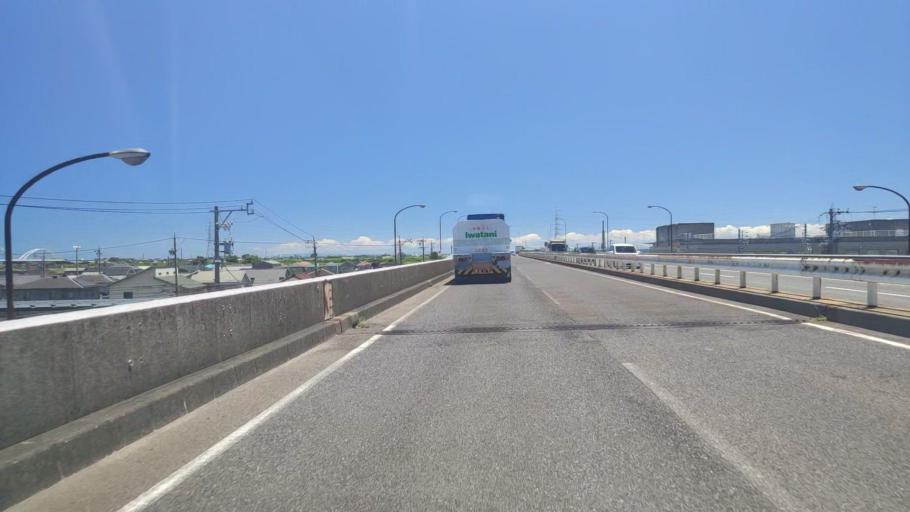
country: JP
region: Mie
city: Yokkaichi
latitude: 34.9284
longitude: 136.6153
